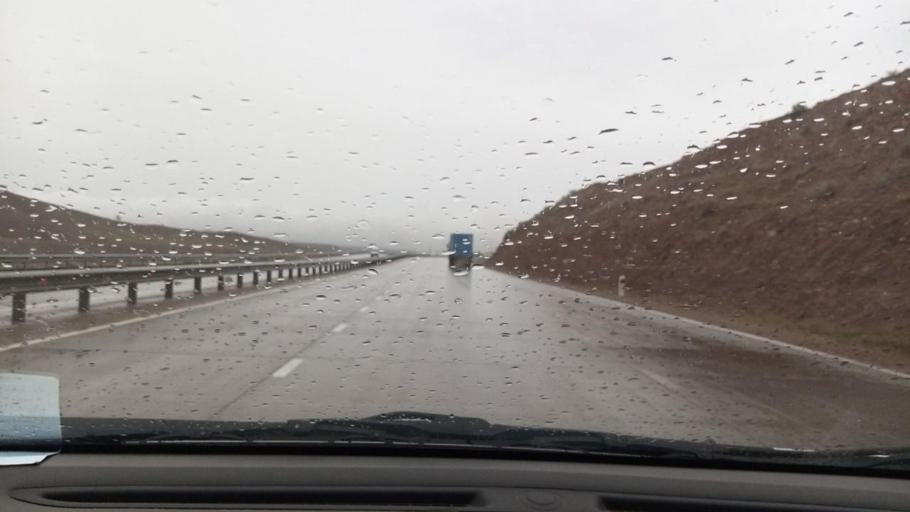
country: UZ
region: Namangan
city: Pop Shahri
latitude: 40.9289
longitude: 70.7118
